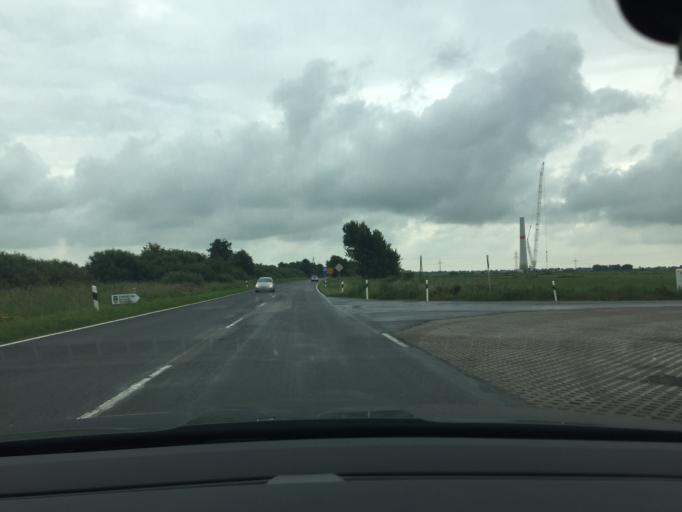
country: DE
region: Lower Saxony
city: Jemgum
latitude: 53.3645
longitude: 7.3472
